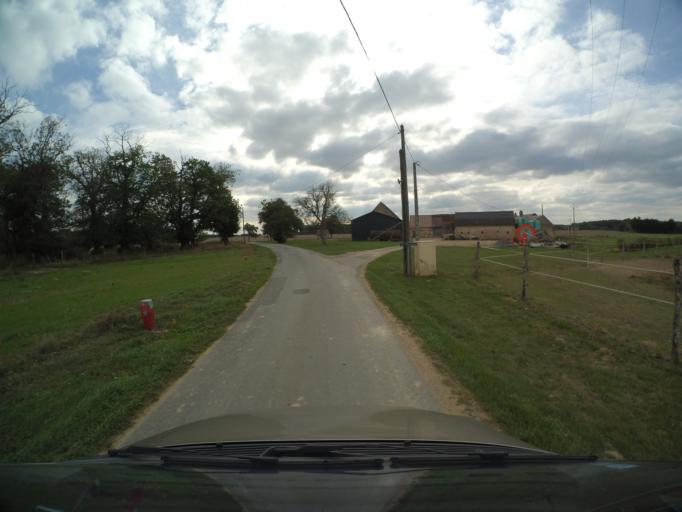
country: FR
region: Centre
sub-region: Departement d'Indre-et-Loire
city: Nazelles-Negron
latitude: 47.4705
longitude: 0.9392
